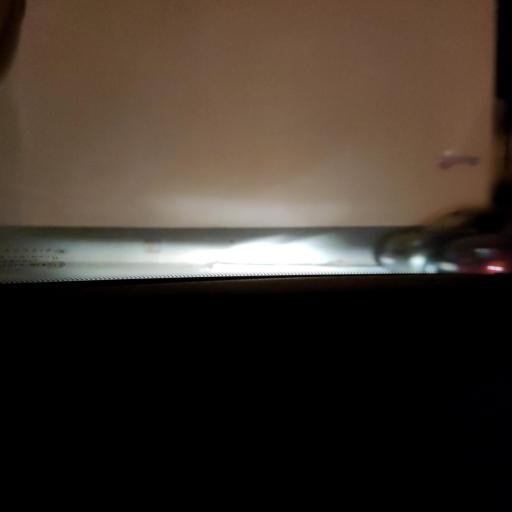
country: RU
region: Samara
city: Samara
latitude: 53.2682
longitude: 50.2233
